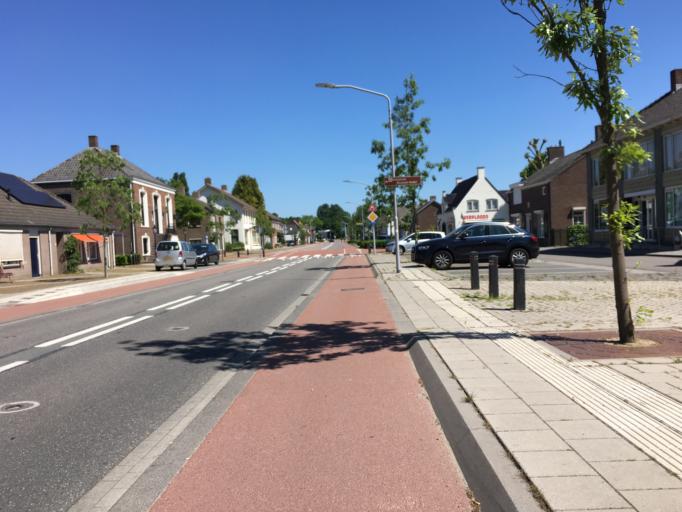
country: NL
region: Gelderland
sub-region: Gemeente Maasdriel
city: Hedel
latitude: 51.7435
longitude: 5.2622
